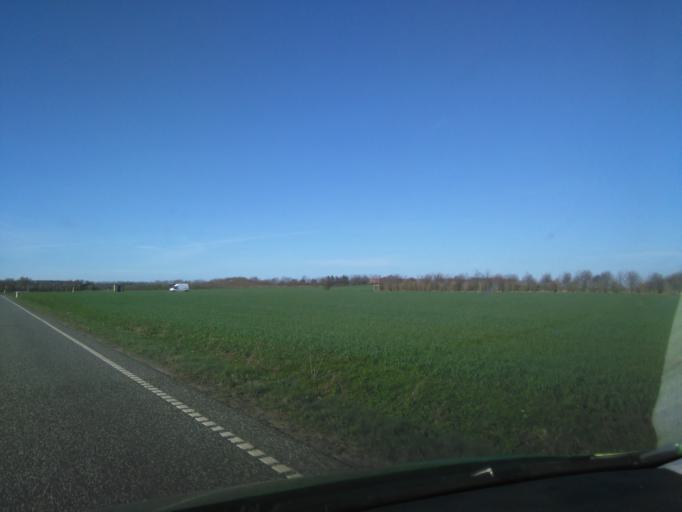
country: DK
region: Central Jutland
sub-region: Ringkobing-Skjern Kommune
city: Skjern
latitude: 56.0724
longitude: 8.5066
